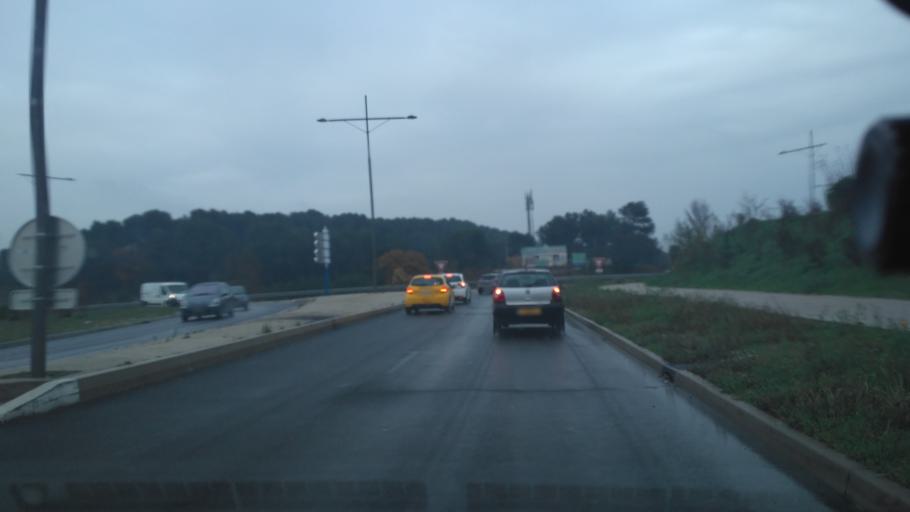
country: FR
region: Languedoc-Roussillon
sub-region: Departement de l'Herault
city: Clapiers
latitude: 43.6528
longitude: 3.8722
